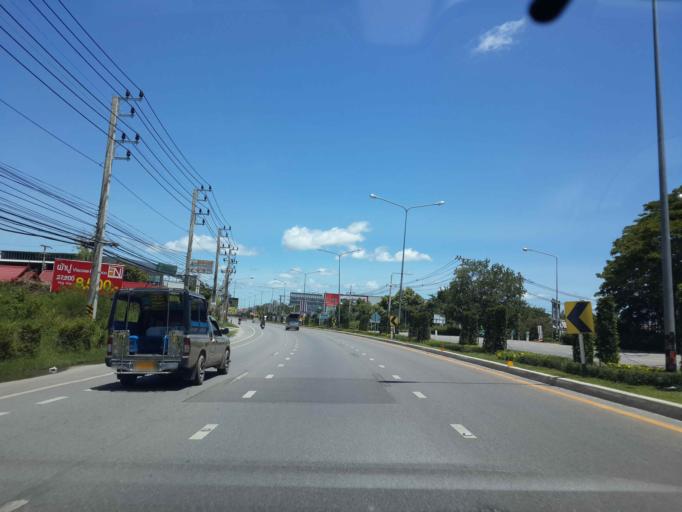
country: TH
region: Prachuap Khiri Khan
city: Hua Hin
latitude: 12.6288
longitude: 99.9509
